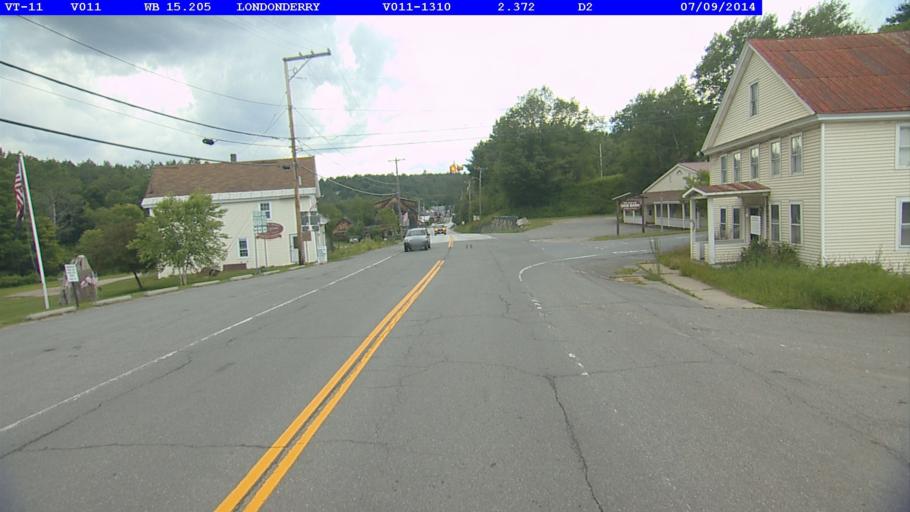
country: US
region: Vermont
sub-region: Windsor County
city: Chester
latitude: 43.2267
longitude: -72.8073
